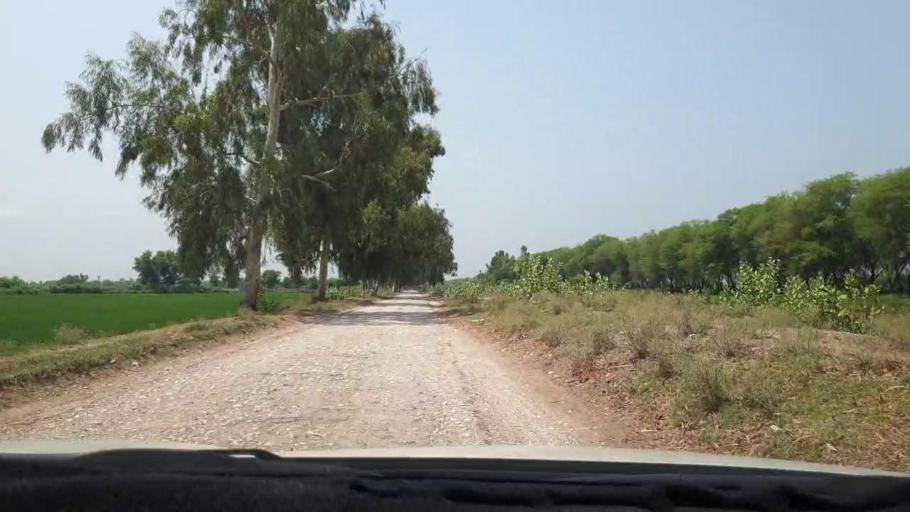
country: PK
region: Sindh
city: Dokri
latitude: 27.3054
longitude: 68.0947
